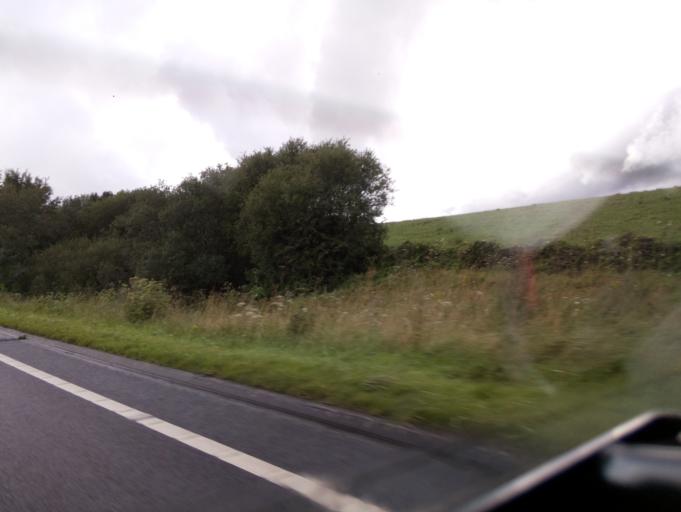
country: GB
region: England
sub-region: Devon
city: South Brent
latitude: 50.4225
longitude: -3.8174
